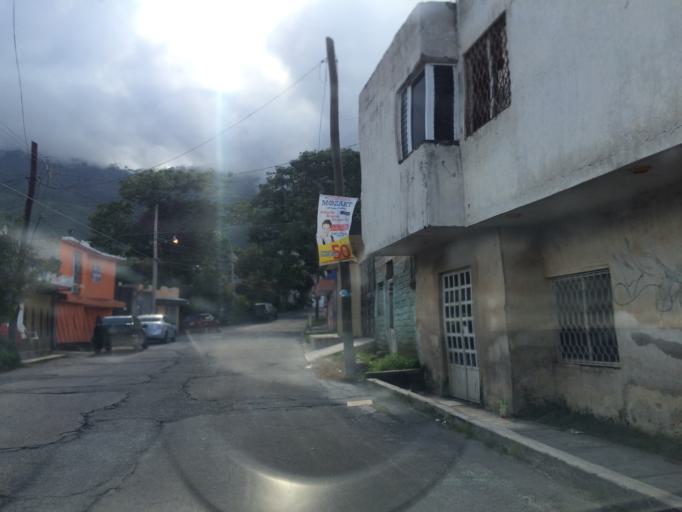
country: MX
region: Nayarit
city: Tepic
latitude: 21.4995
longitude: -104.9127
